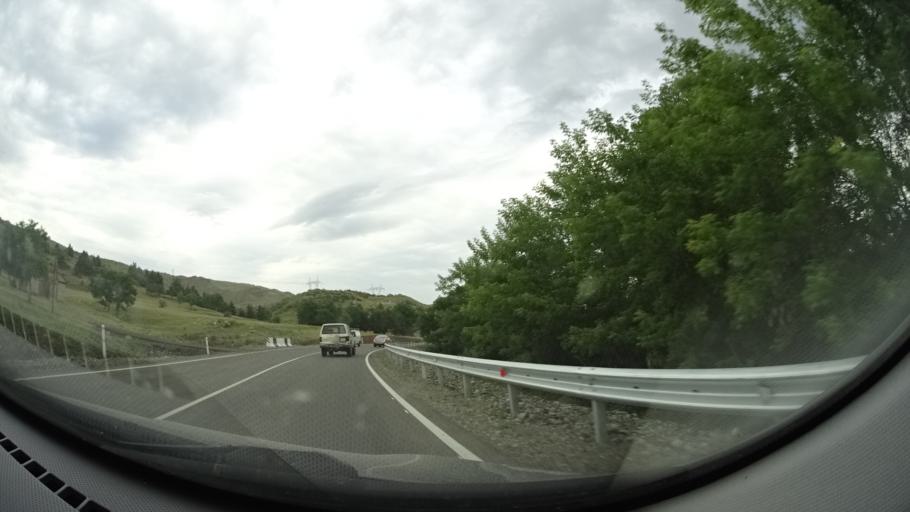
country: GE
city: Vale
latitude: 41.6490
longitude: 42.8614
